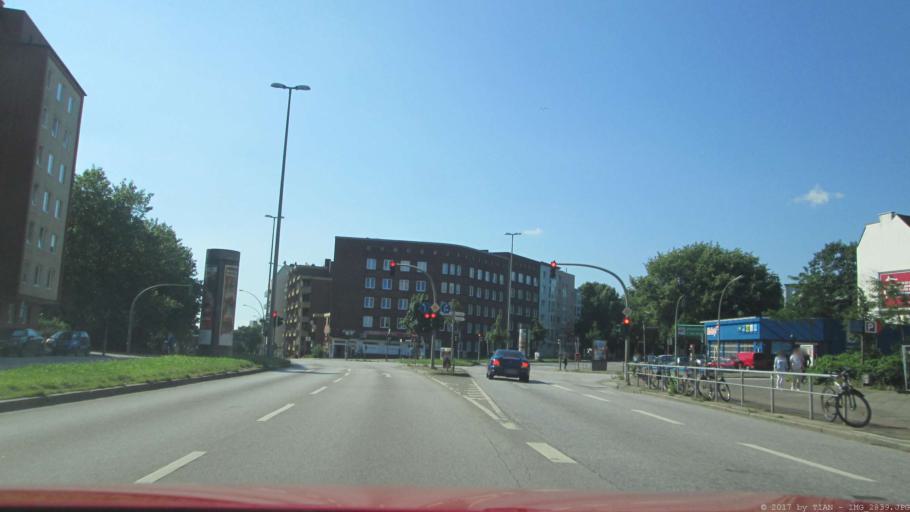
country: DE
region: Hamburg
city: Wandsbek
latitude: 53.5422
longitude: 10.0968
